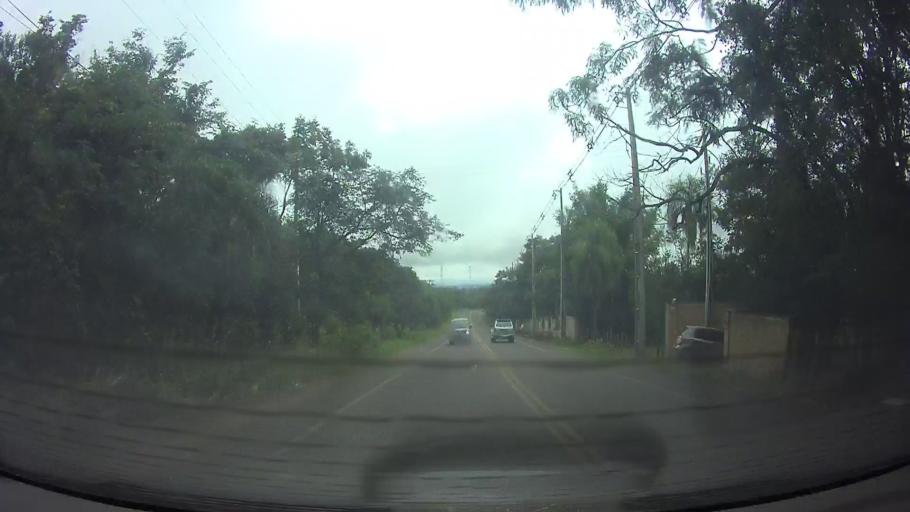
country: PY
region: Cordillera
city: Altos
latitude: -25.2840
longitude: -57.2620
